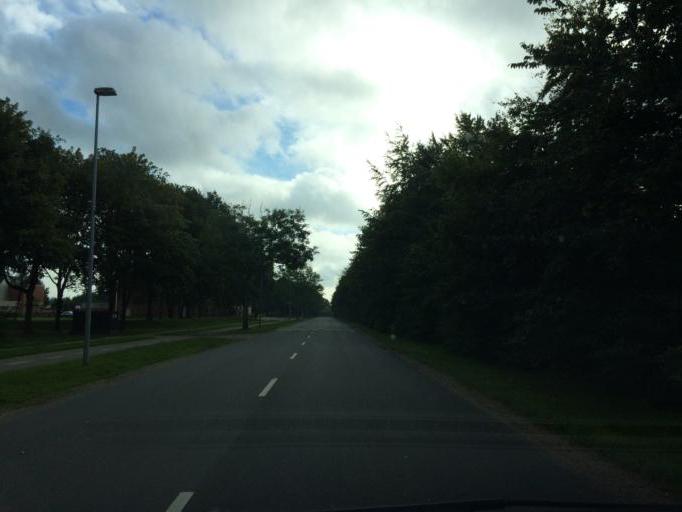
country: DK
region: North Denmark
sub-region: Bronderslev Kommune
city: Dronninglund
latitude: 57.1541
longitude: 10.2759
